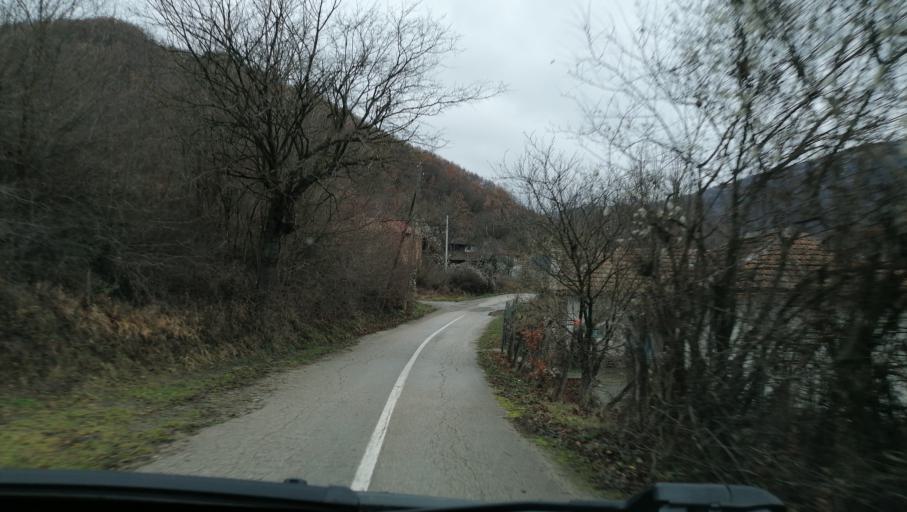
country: RS
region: Central Serbia
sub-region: Pirotski Okrug
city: Dimitrovgrad
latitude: 42.9775
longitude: 22.7843
